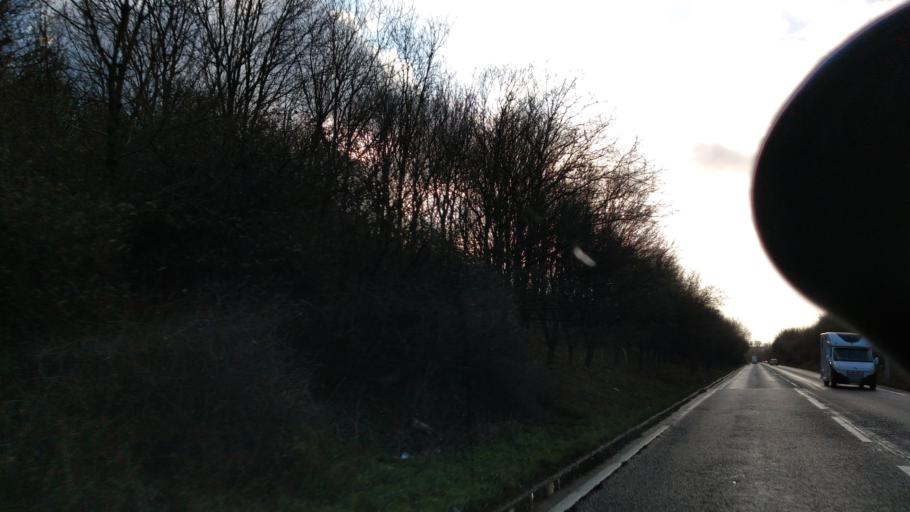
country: GB
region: England
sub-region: Somerset
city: Frome
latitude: 51.2235
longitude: -2.3023
